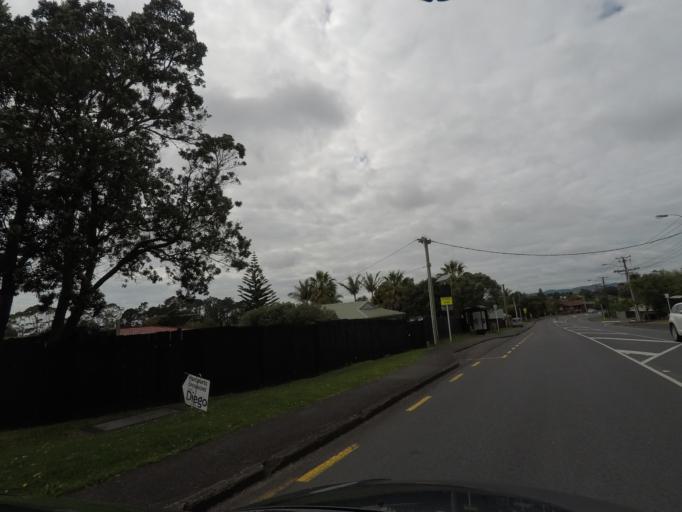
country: NZ
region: Auckland
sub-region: Auckland
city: Rosebank
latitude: -36.8493
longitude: 174.6095
